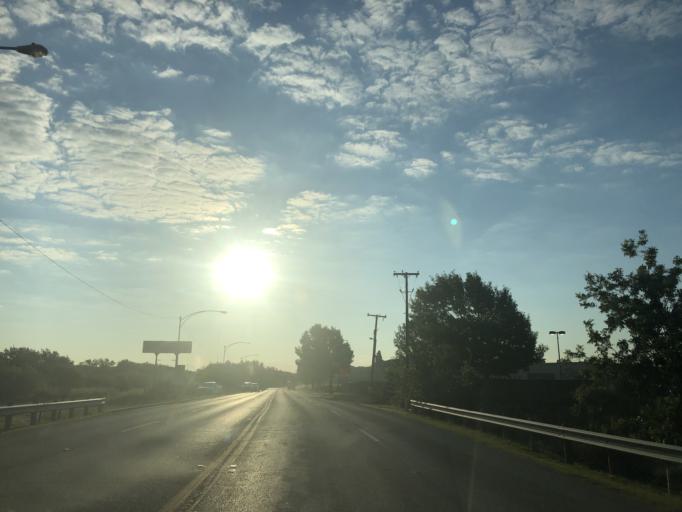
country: US
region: Texas
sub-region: Dallas County
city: Grand Prairie
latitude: 32.7616
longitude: -96.9995
